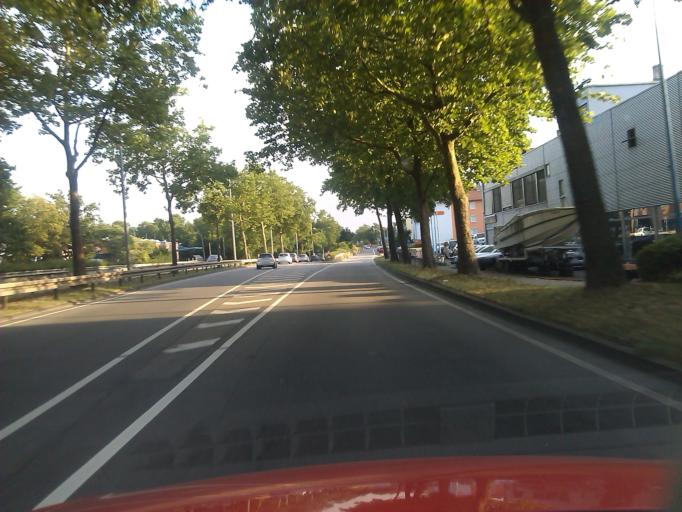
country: DE
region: Baden-Wuerttemberg
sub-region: Regierungsbezirk Stuttgart
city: Heilbronn
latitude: 49.1452
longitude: 9.1997
